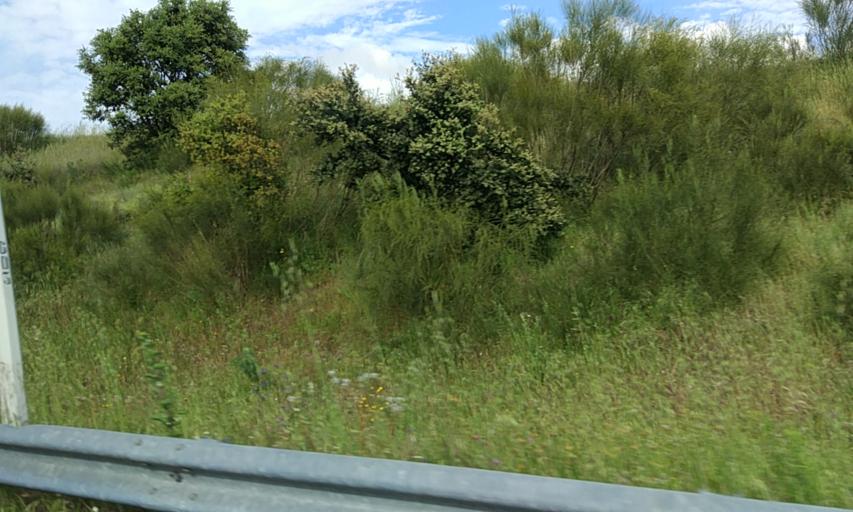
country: PT
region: Evora
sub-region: Evora
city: Evora
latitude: 38.6460
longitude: -7.8562
